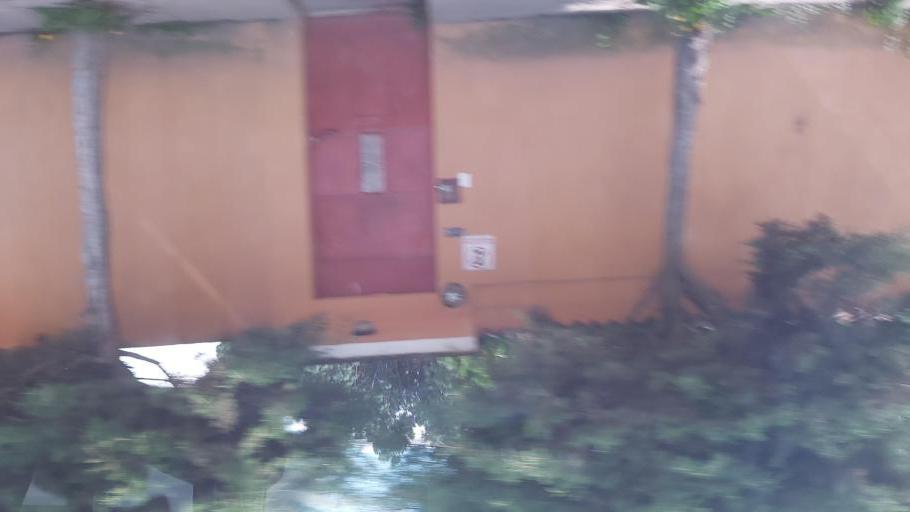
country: GT
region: Quetzaltenango
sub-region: Municipio de La Esperanza
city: La Esperanza
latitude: 14.8554
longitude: -91.5447
